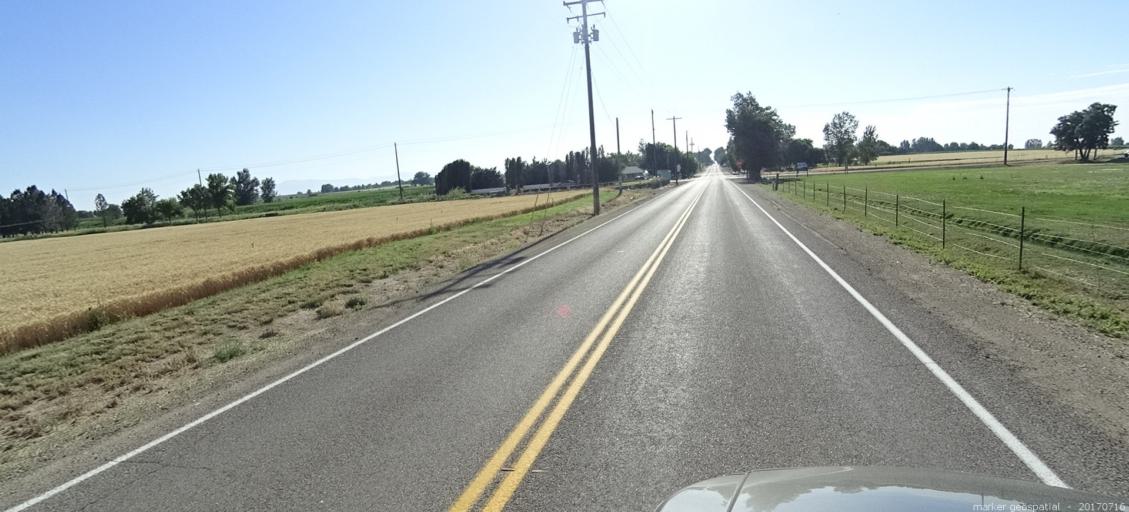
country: US
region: Idaho
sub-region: Ada County
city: Kuna
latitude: 43.5466
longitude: -116.4355
